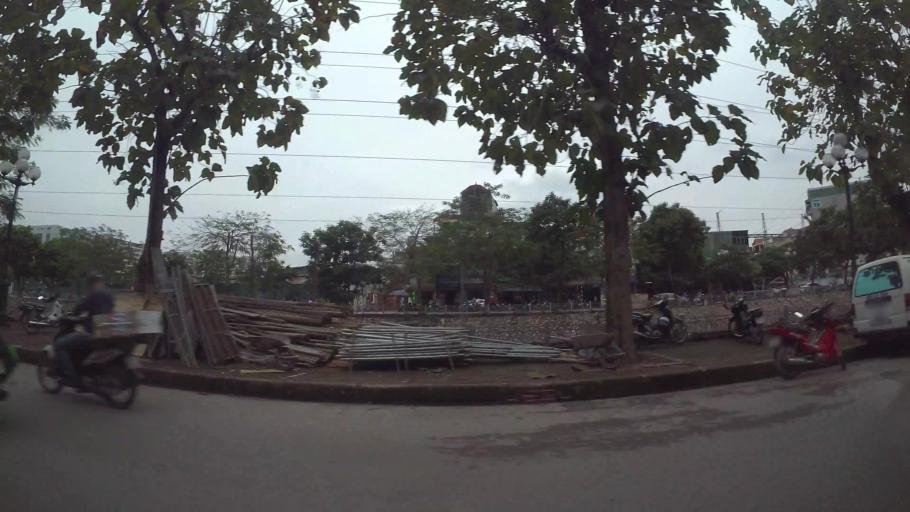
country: VN
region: Ha Noi
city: Hai BaTrung
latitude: 21.0063
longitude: 105.8614
